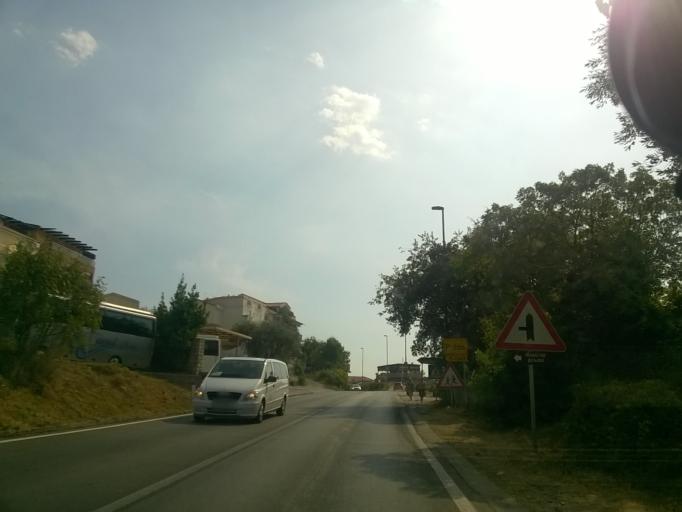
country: ME
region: Budva
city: Budva
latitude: 42.2728
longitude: 18.8911
